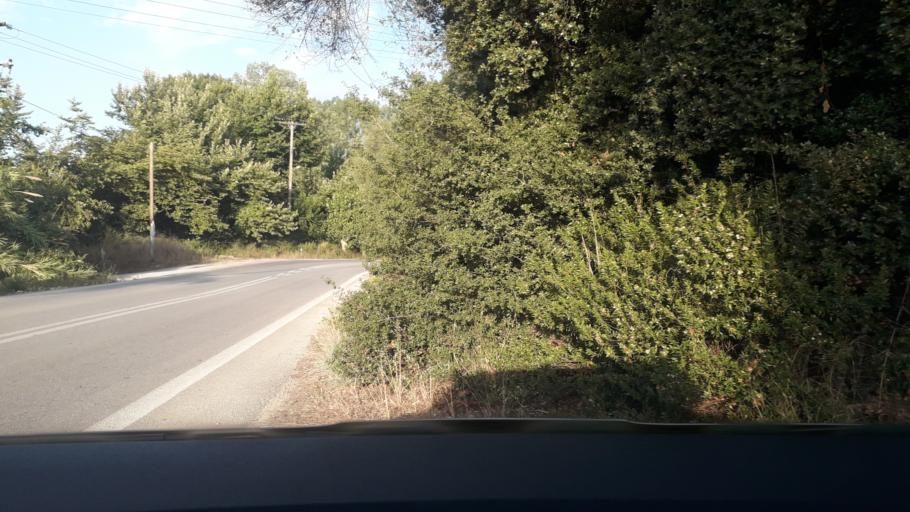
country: GR
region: Ionian Islands
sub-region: Nomos Kerkyras
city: Agios Matthaios
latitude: 39.4770
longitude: 19.9213
